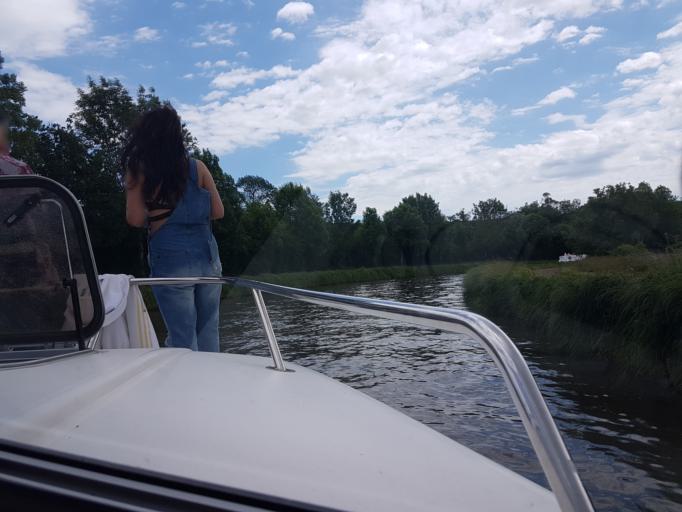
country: FR
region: Bourgogne
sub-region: Departement de la Nievre
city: Clamecy
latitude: 47.4908
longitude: 3.5234
